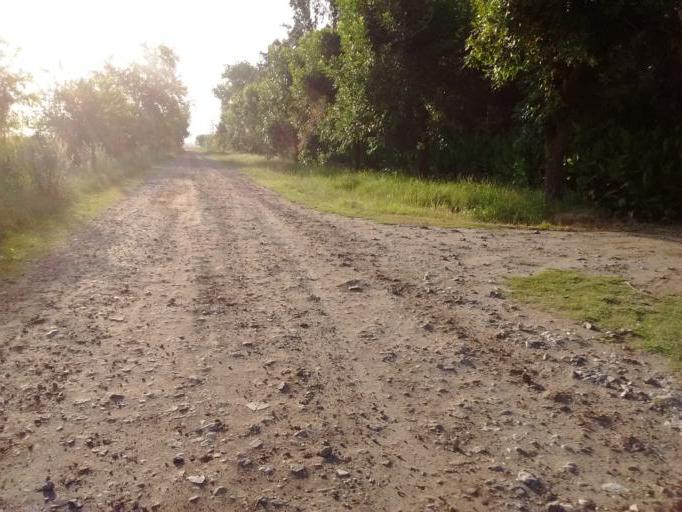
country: AR
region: Santa Fe
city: Roldan
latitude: -32.9309
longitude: -60.8641
